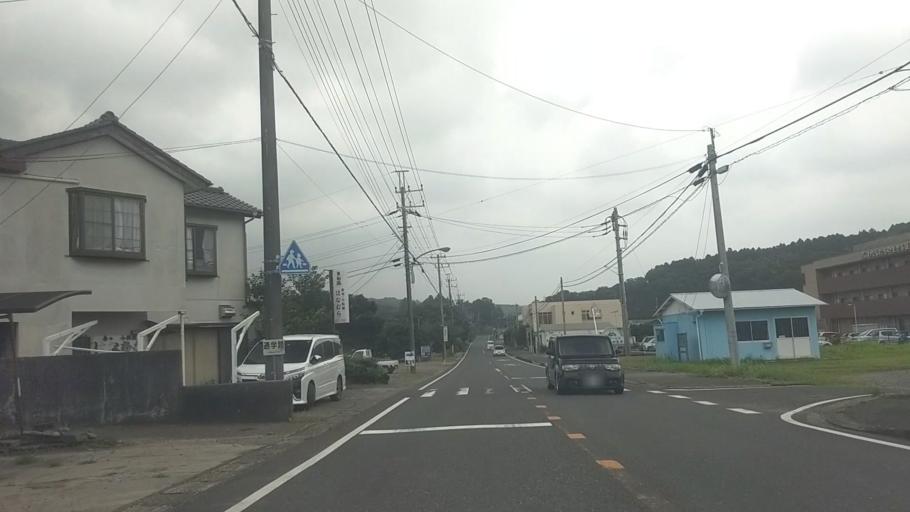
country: JP
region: Chiba
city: Kimitsu
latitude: 35.2189
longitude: 139.9045
